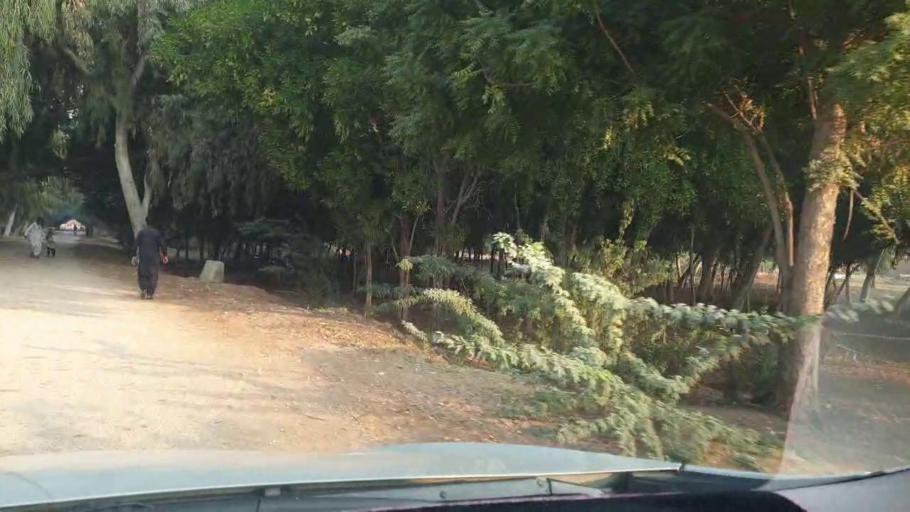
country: PK
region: Sindh
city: Sehwan
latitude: 26.3954
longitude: 67.8622
